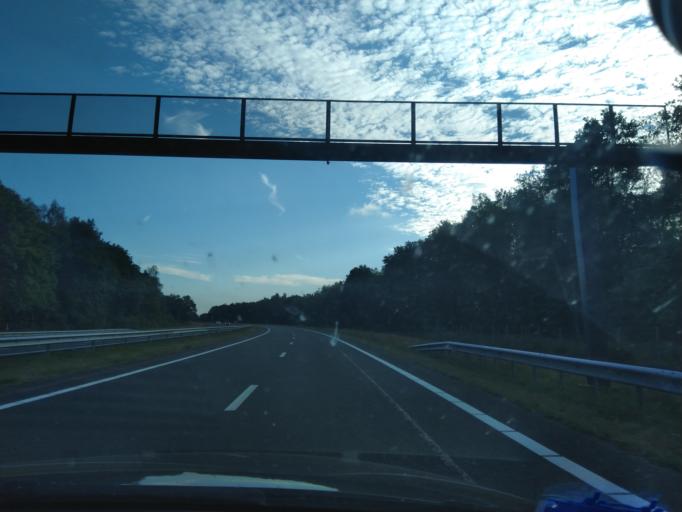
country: NL
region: Drenthe
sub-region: Gemeente Aa en Hunze
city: Anloo
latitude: 52.9997
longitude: 6.7013
